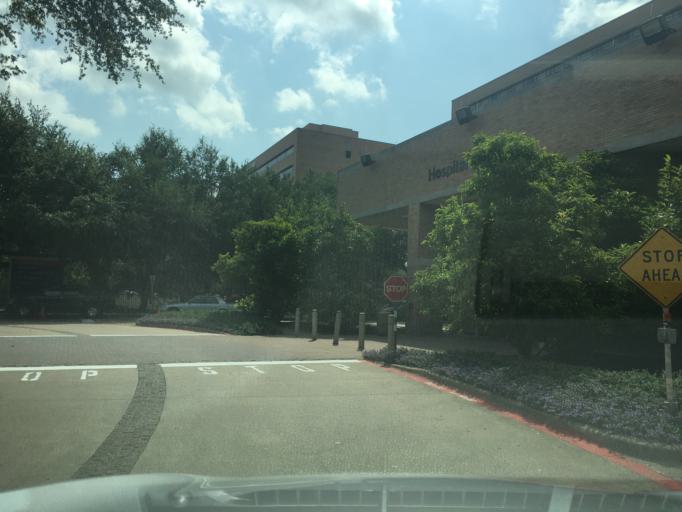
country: US
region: Texas
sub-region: Dallas County
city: University Park
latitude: 32.8820
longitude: -96.7631
